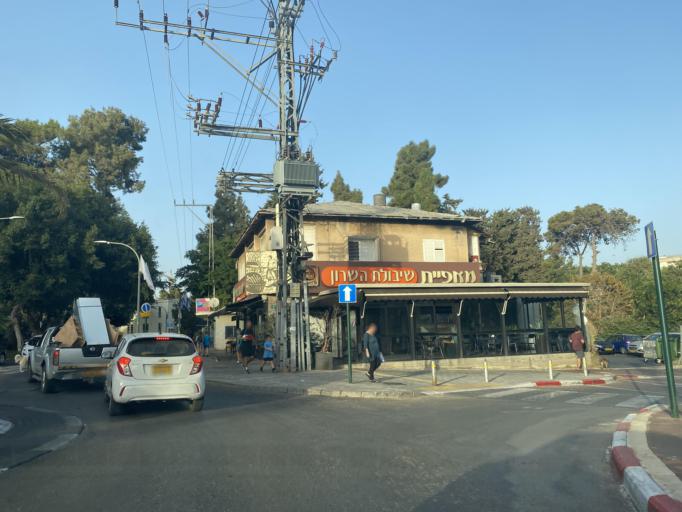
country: IL
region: Central District
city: Hod HaSharon
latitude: 32.1597
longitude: 34.9021
